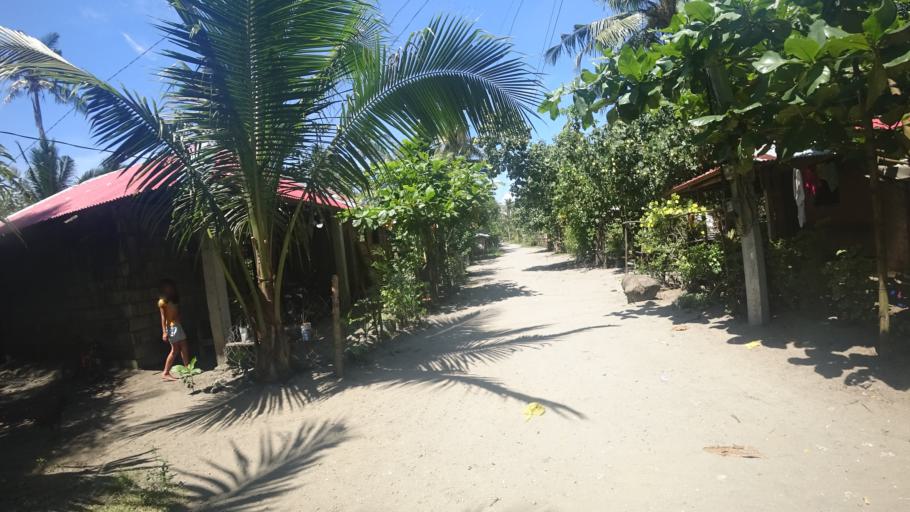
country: PH
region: Eastern Visayas
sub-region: Province of Leyte
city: Mayorga
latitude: 10.8891
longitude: 125.0128
